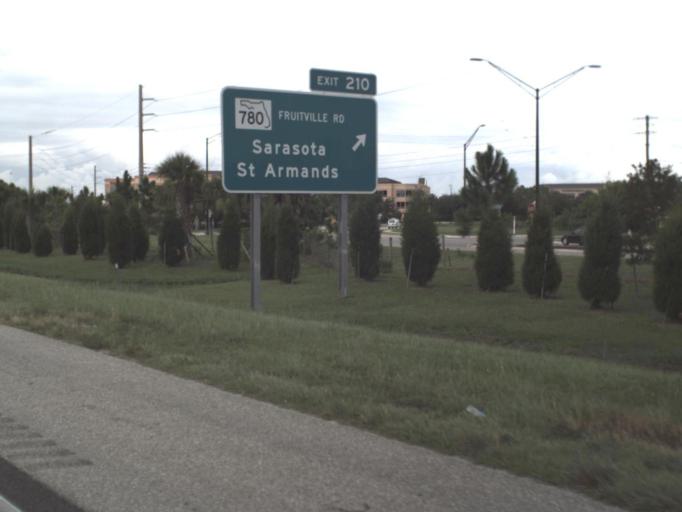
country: US
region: Florida
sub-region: Sarasota County
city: Fruitville
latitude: 27.3449
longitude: -82.4469
